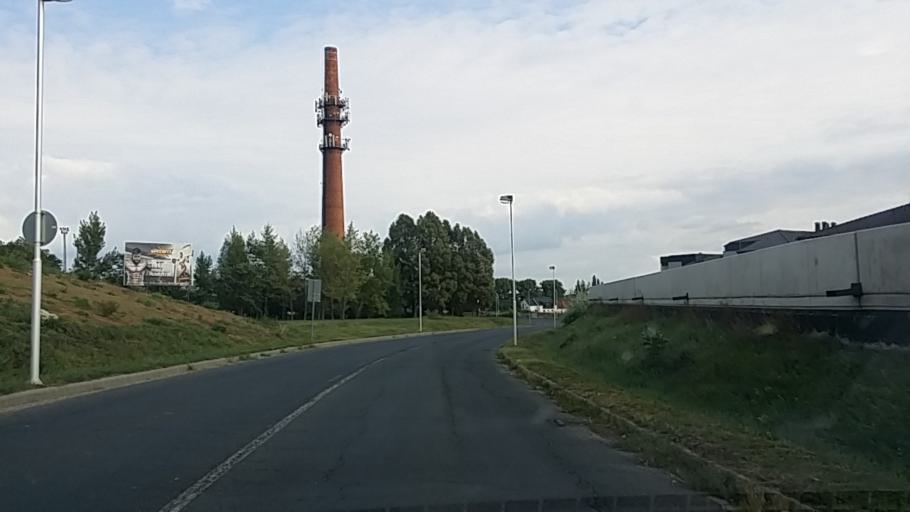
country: HU
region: Gyor-Moson-Sopron
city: Sopron
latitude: 47.6862
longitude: 16.6075
